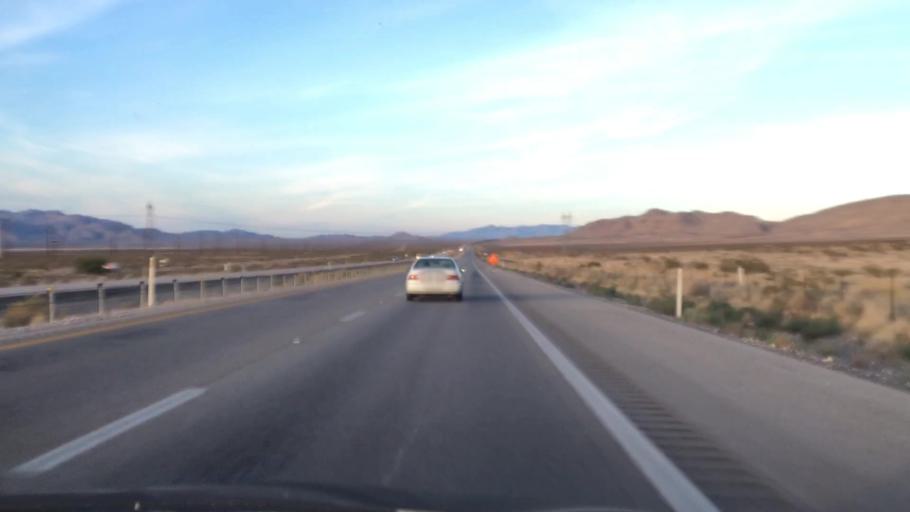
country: US
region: Nevada
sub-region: Clark County
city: Nellis Air Force Base
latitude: 36.3988
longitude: -114.8804
